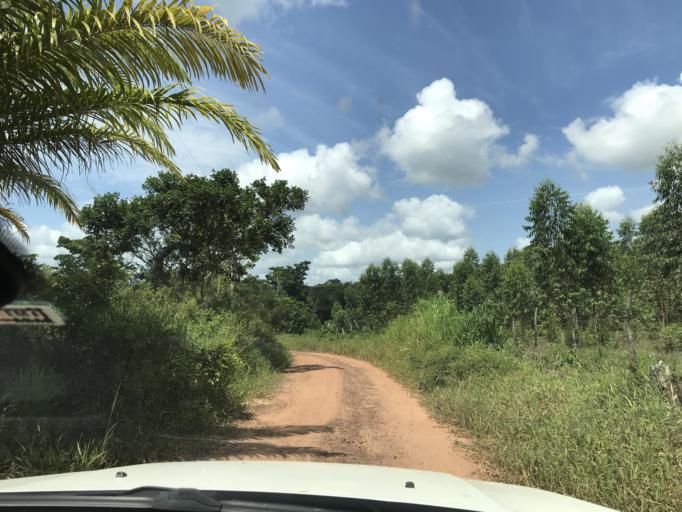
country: BR
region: Bahia
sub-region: Entre Rios
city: Entre Rios
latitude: -12.2184
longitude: -38.0784
